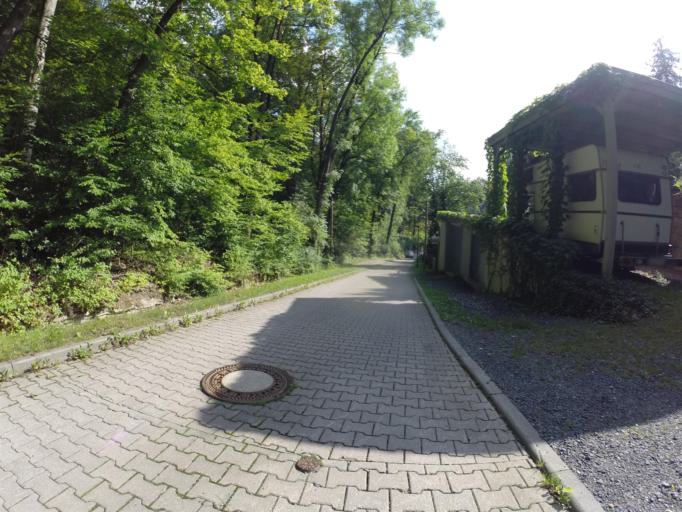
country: DE
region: Thuringia
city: Jena
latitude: 50.9390
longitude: 11.5761
